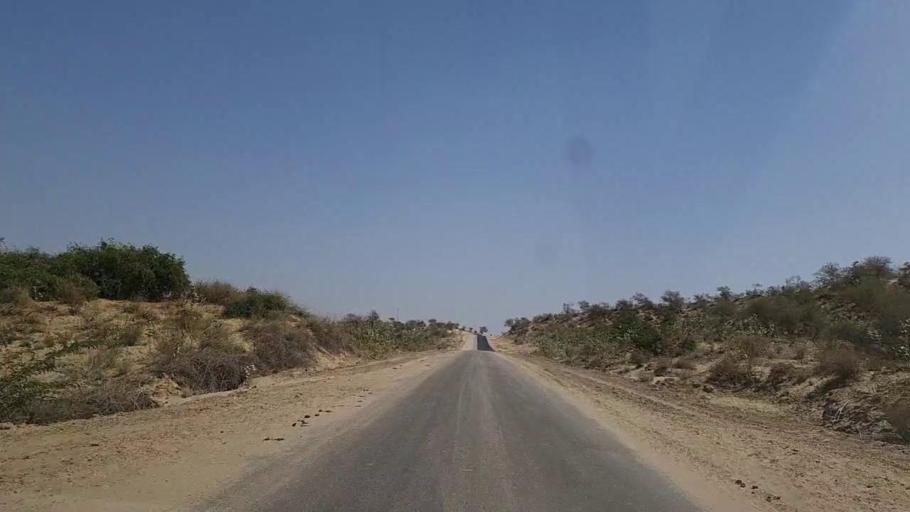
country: PK
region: Sindh
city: Diplo
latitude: 24.4812
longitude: 69.4901
